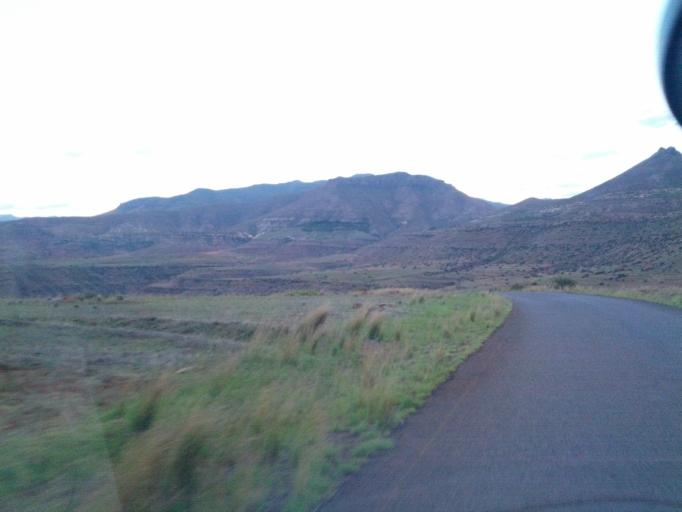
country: LS
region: Qacha's Nek
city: Qacha's Nek
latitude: -30.0581
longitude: 28.3811
